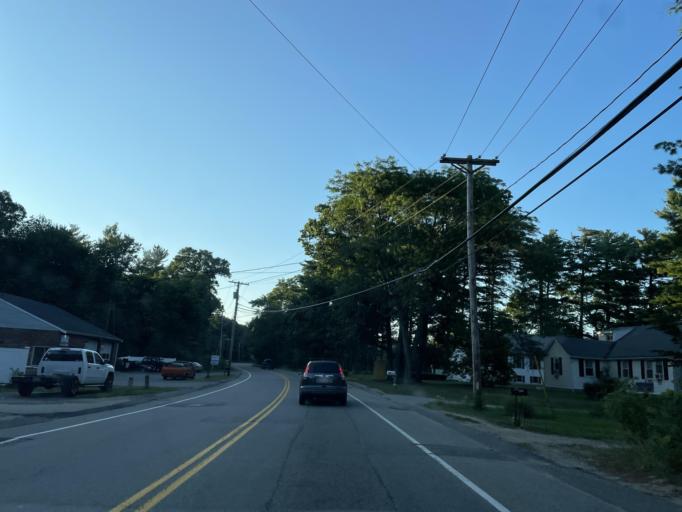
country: US
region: Massachusetts
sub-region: Plymouth County
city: Halifax
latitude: 42.0256
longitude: -70.8426
